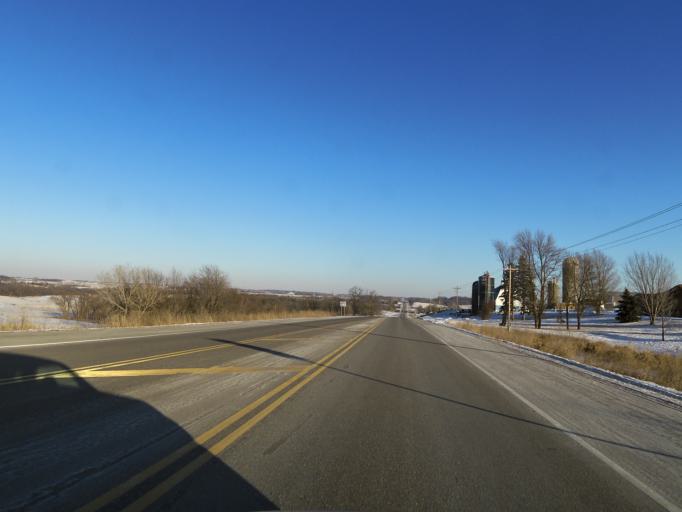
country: US
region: Minnesota
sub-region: Rice County
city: Lonsdale
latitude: 44.5437
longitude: -93.4188
